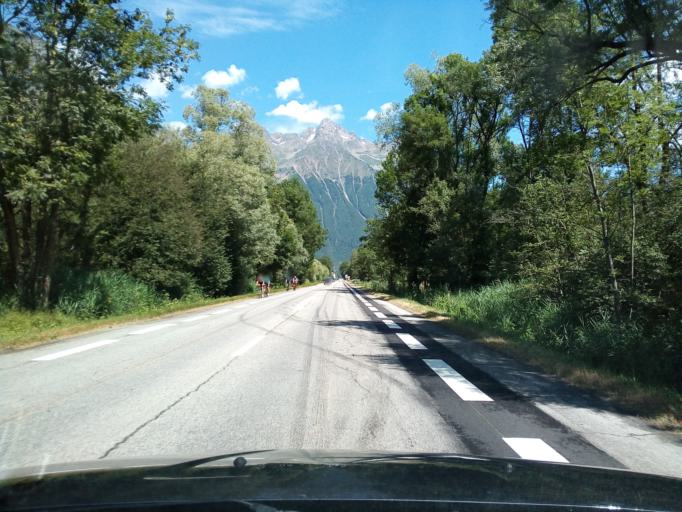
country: FR
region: Rhone-Alpes
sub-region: Departement de l'Isere
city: Huez
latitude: 45.0856
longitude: 6.0126
